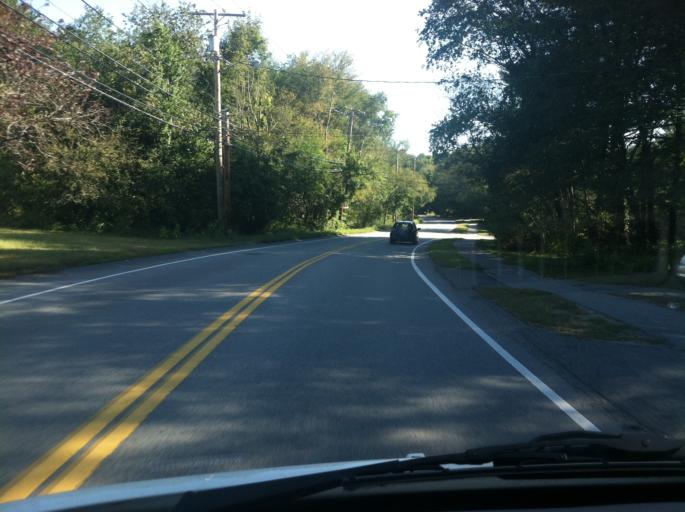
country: US
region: Massachusetts
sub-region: Middlesex County
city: Bedford
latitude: 42.4873
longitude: -71.2947
